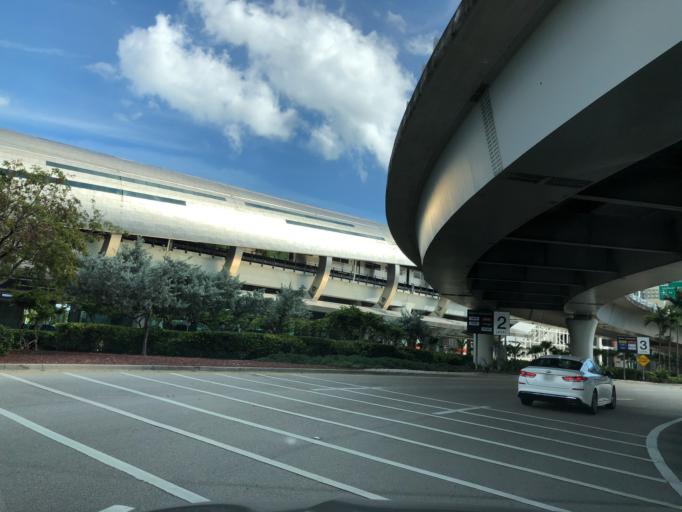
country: US
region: Florida
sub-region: Miami-Dade County
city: Brownsville
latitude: 25.7985
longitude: -80.2593
